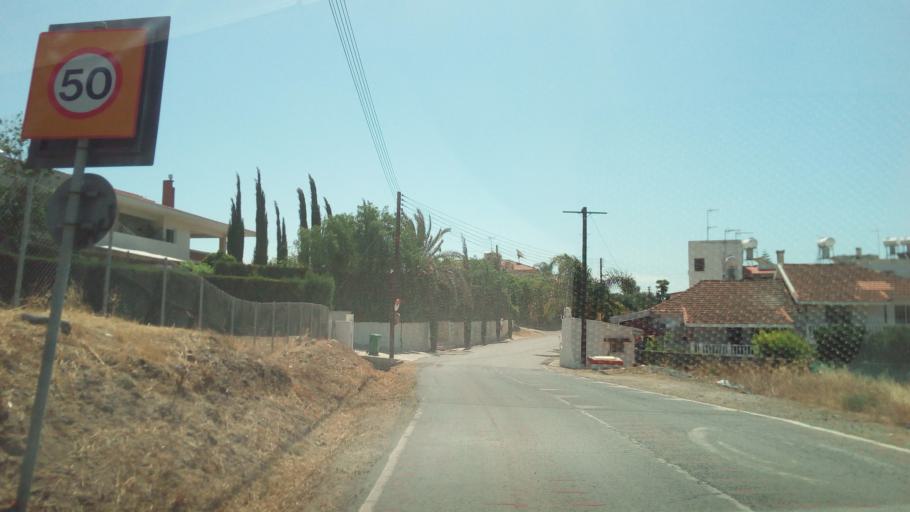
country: CY
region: Limassol
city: Pyrgos
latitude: 34.7435
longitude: 33.1789
